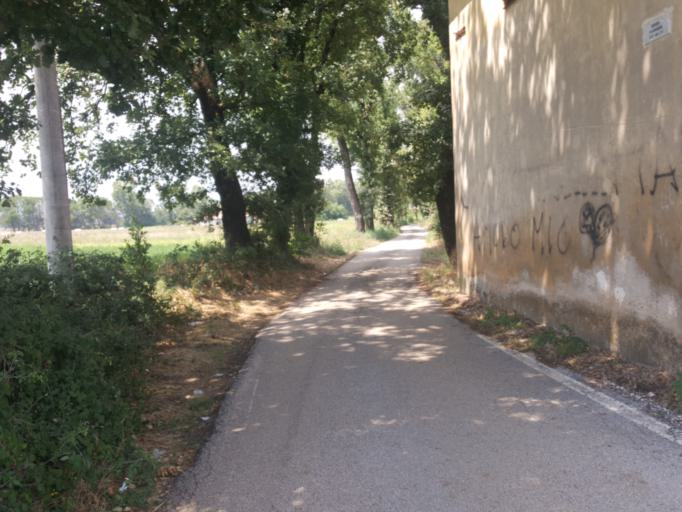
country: IT
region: Latium
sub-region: Provincia di Frosinone
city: Aquino
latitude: 41.5023
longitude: 13.6836
